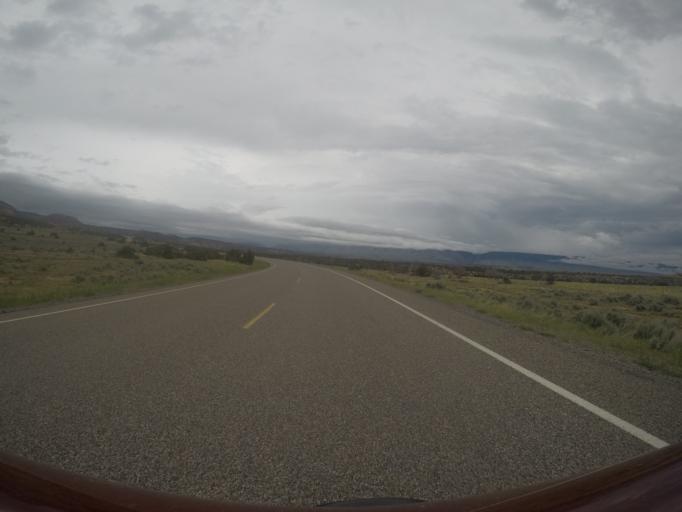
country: US
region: Wyoming
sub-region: Big Horn County
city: Lovell
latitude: 45.0844
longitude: -108.2526
